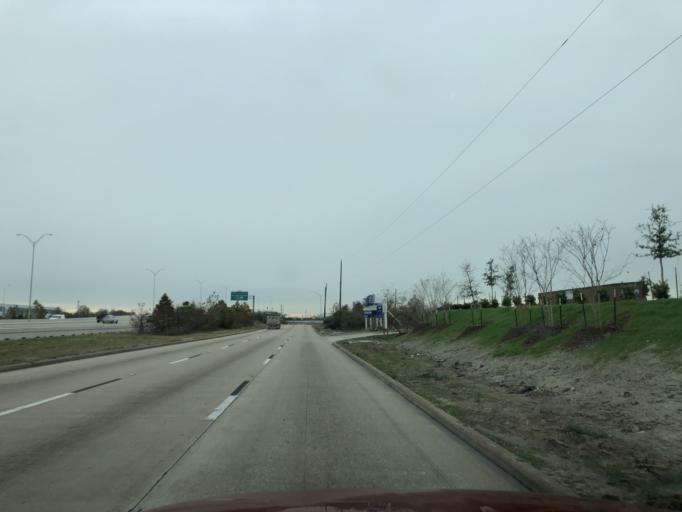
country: US
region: Texas
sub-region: Fort Bend County
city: Missouri City
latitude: 29.6298
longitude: -95.5228
